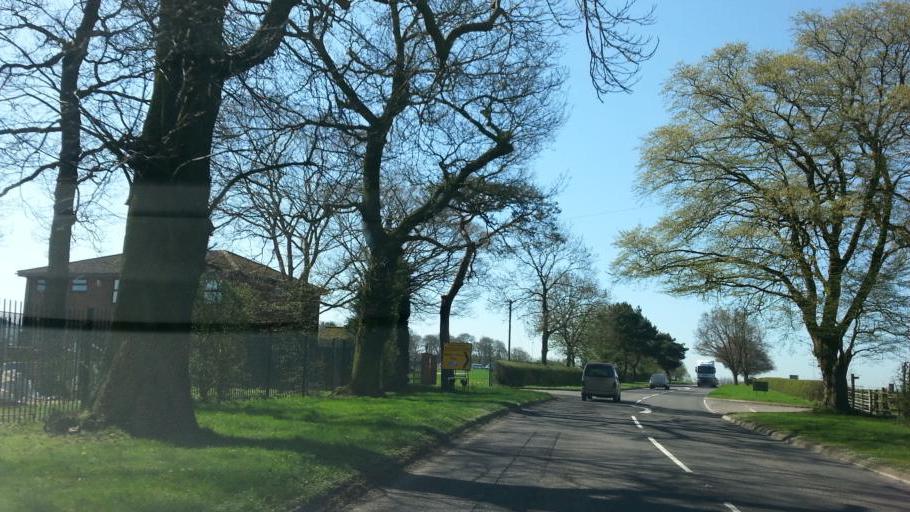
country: GB
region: England
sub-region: Staffordshire
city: Stafford
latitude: 52.8280
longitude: -2.0661
